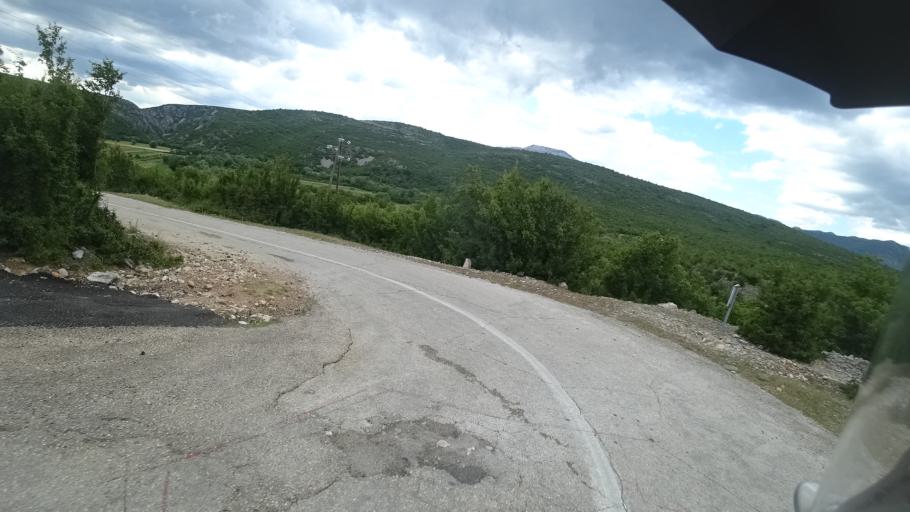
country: HR
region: Zadarska
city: Gracac
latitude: 44.1893
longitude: 15.8888
